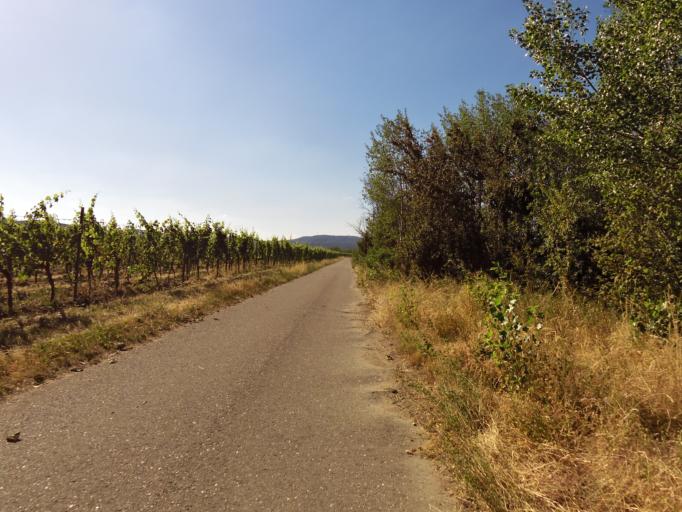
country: DE
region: Rheinland-Pfalz
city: Friedelsheim
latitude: 49.4346
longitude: 8.2081
